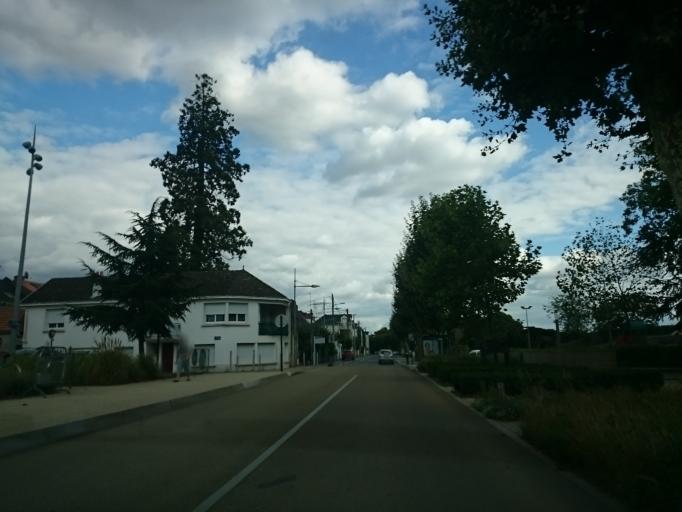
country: FR
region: Pays de la Loire
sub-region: Departement de la Loire-Atlantique
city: Indre
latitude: 47.1978
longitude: -1.6725
